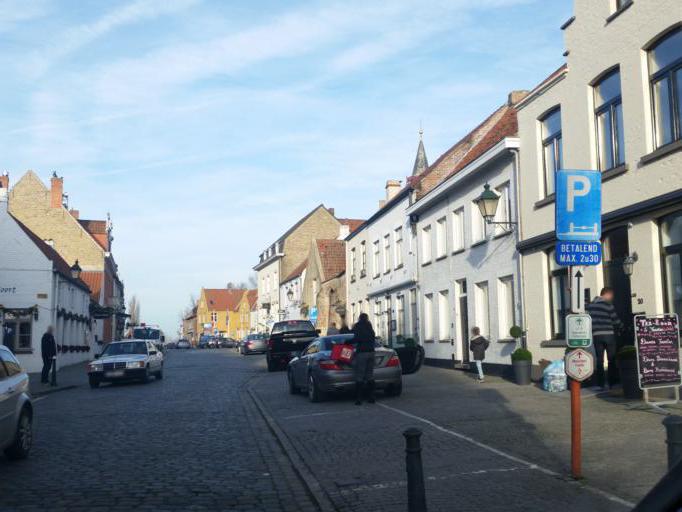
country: BE
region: Flanders
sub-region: Provincie West-Vlaanderen
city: Damme
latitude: 51.2506
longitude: 3.2820
